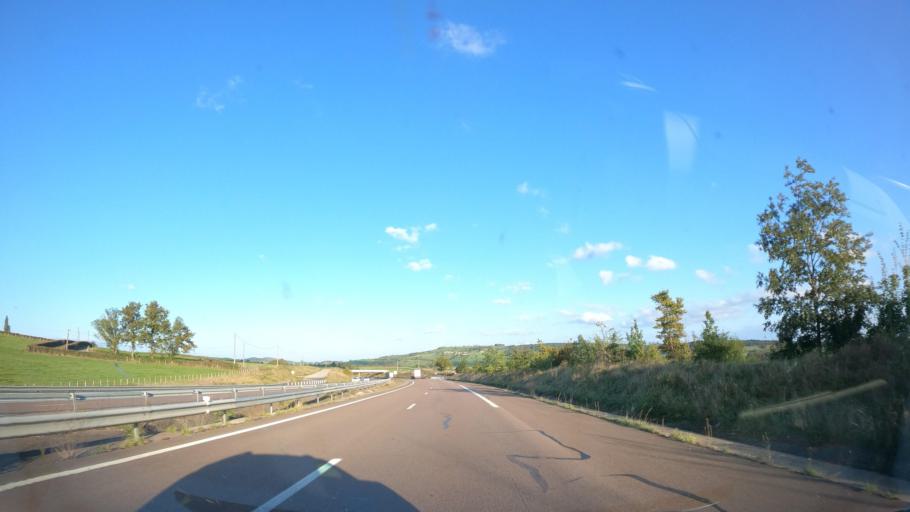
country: FR
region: Bourgogne
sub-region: Departement de Saone-et-Loire
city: Ecuisses
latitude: 46.7373
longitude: 4.6183
